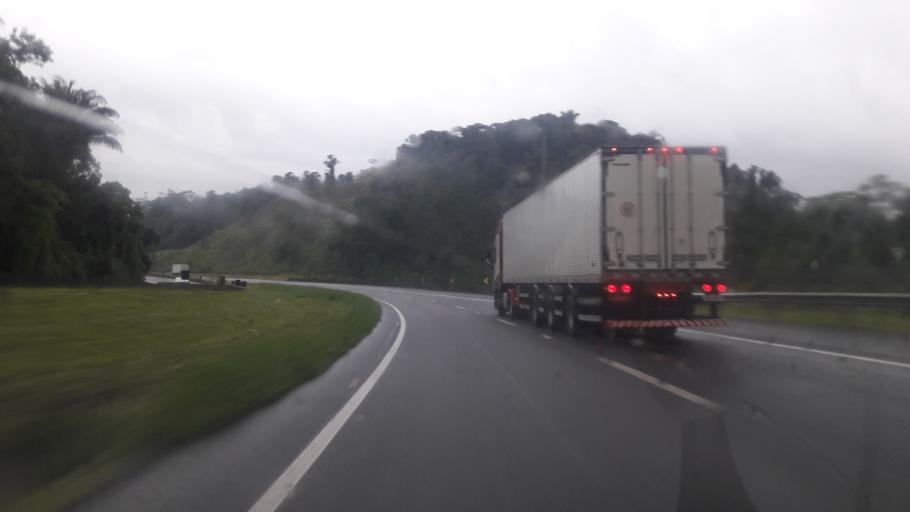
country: BR
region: Sao Paulo
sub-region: Cajati
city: Cajati
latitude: -24.9723
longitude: -48.3510
